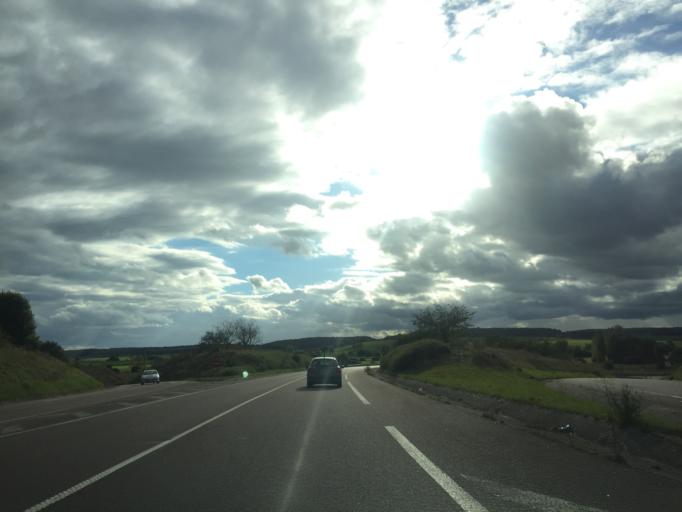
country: FR
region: Lorraine
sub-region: Departement des Vosges
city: Chatenois
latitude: 48.2939
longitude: 5.9030
